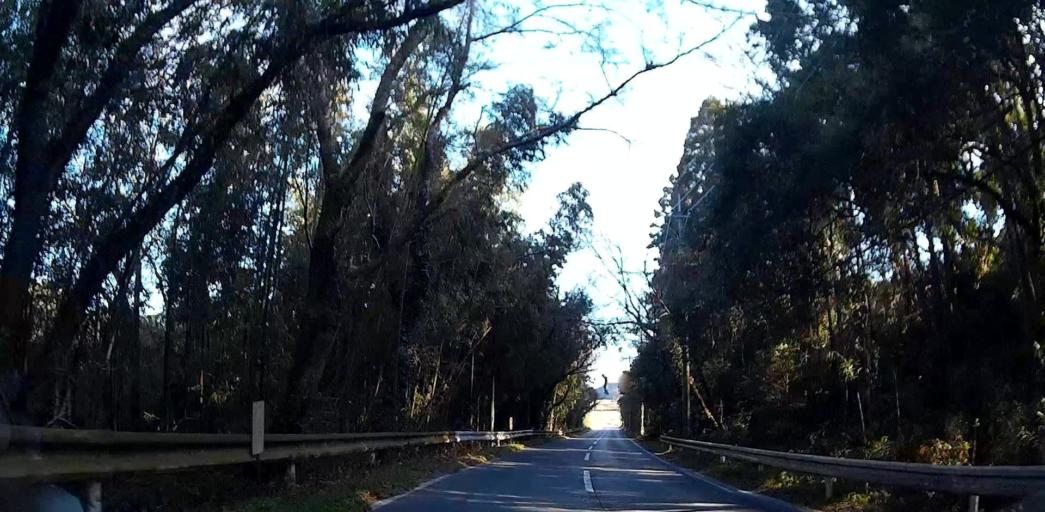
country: JP
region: Chiba
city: Yokaichiba
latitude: 35.7361
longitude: 140.4934
